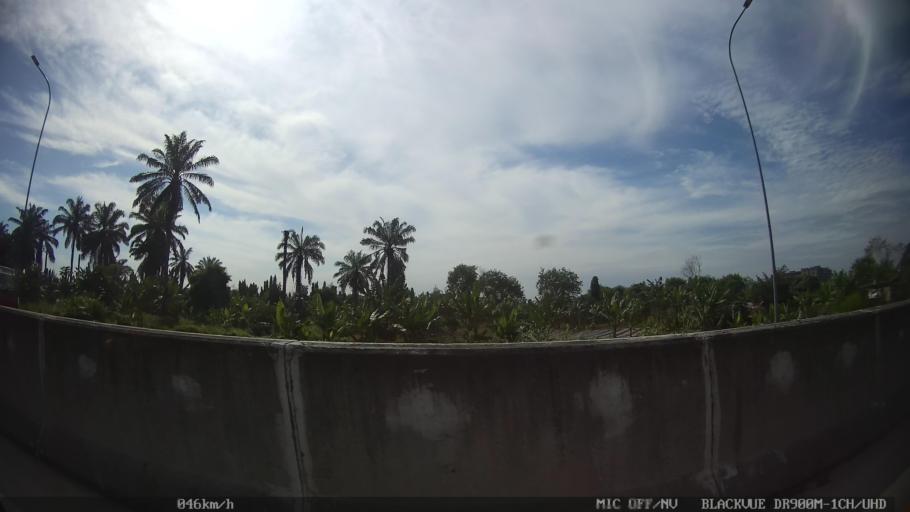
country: ID
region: North Sumatra
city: Sunggal
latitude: 3.6307
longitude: 98.6332
